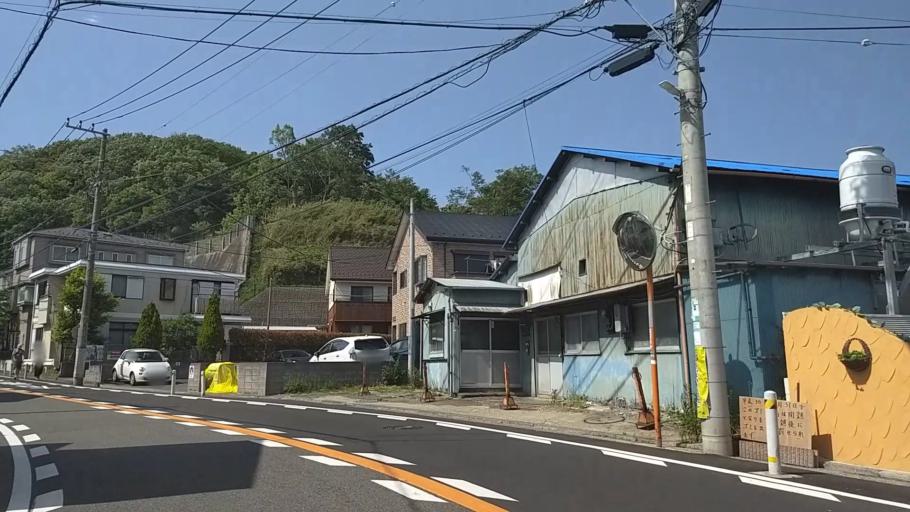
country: JP
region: Kanagawa
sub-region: Kawasaki-shi
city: Kawasaki
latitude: 35.5463
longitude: 139.6422
